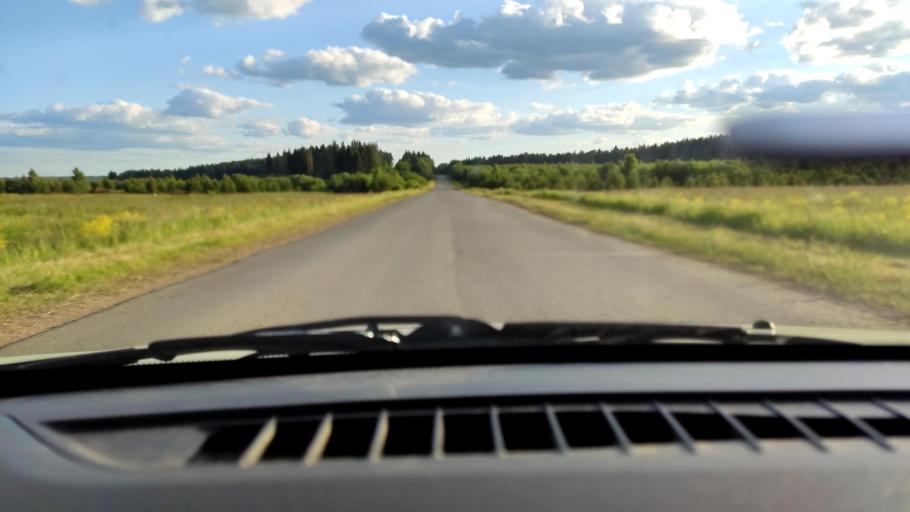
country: RU
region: Perm
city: Uinskoye
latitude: 57.0905
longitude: 56.6322
